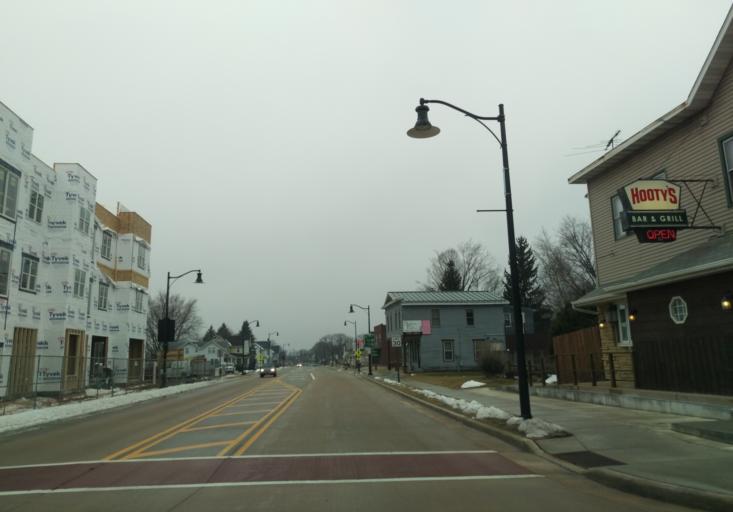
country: US
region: Wisconsin
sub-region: Dane County
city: Cross Plains
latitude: 43.1138
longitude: -89.6504
